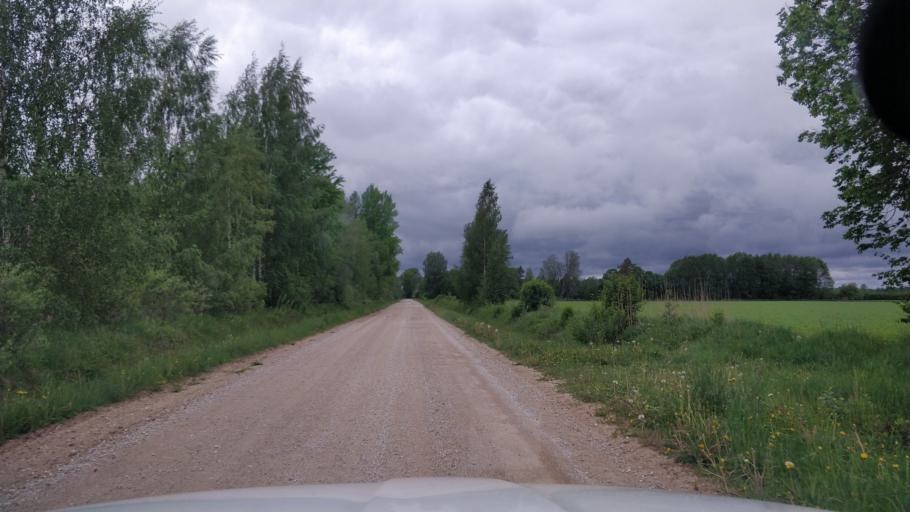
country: EE
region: Raplamaa
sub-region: Maerjamaa vald
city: Marjamaa
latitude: 58.7159
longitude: 24.3066
